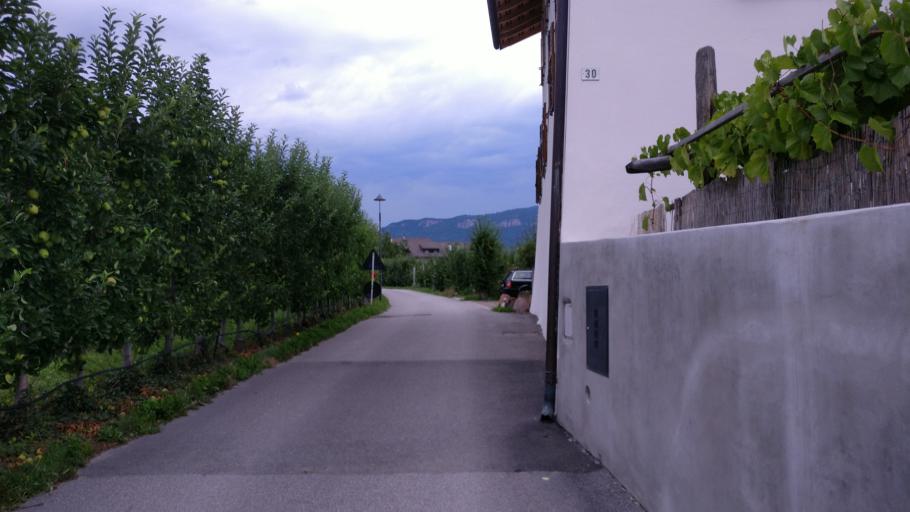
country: IT
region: Trentino-Alto Adige
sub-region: Bolzano
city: San Paolo
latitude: 46.4854
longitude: 11.2551
